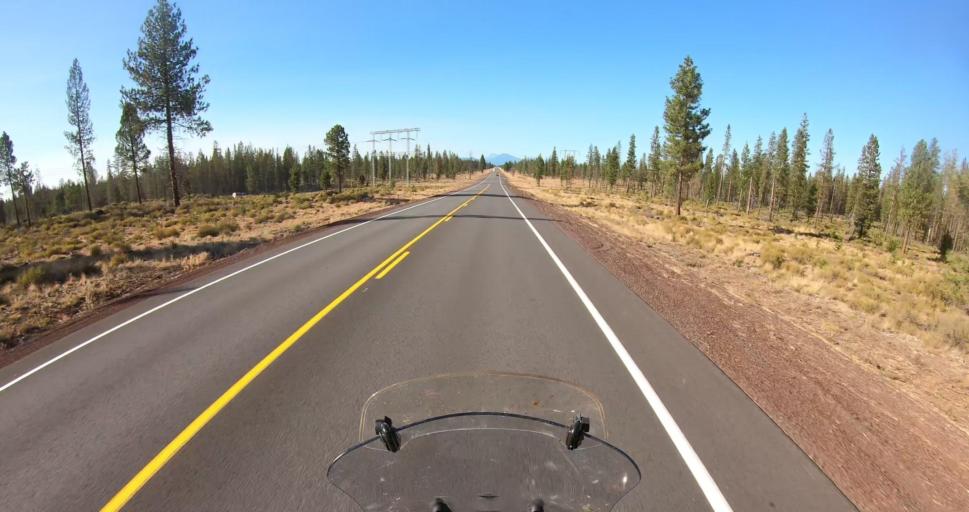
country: US
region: Oregon
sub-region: Deschutes County
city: La Pine
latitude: 43.5611
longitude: -121.4771
